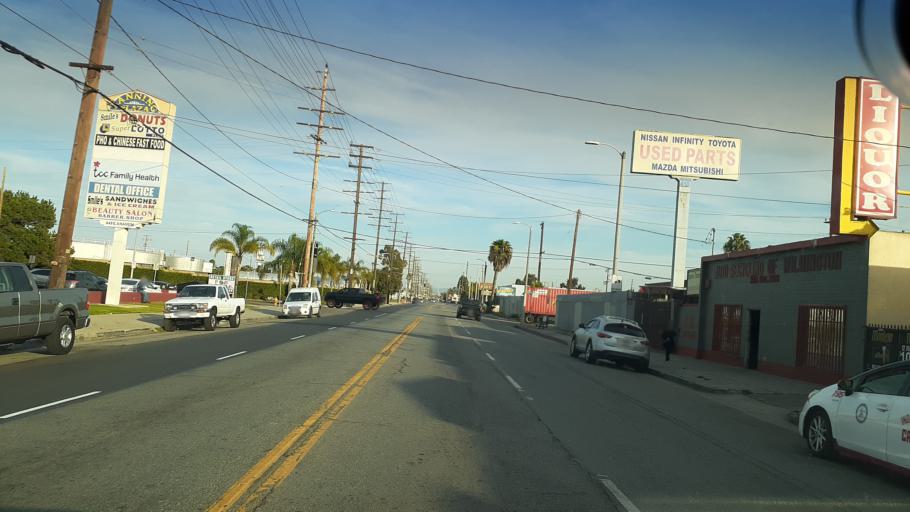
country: US
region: California
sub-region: Los Angeles County
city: West Carson
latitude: 33.7802
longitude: -118.2581
